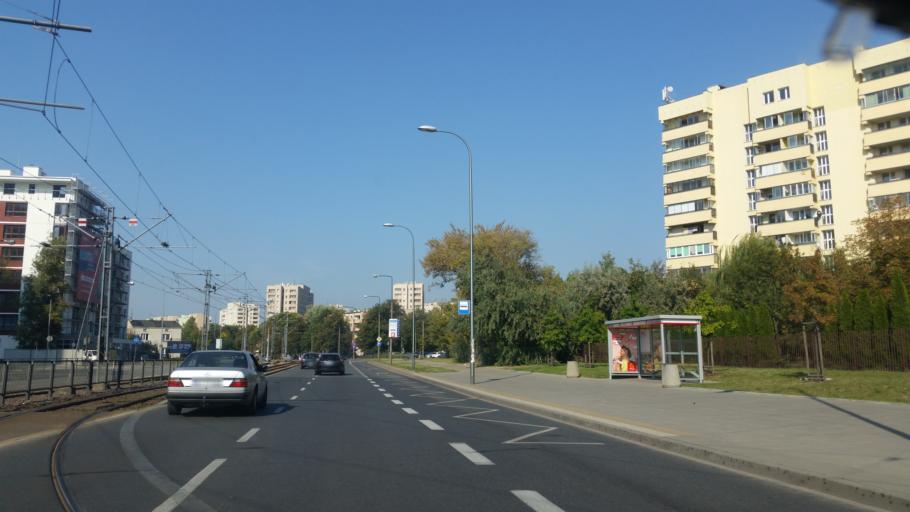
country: PL
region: Masovian Voivodeship
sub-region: Warszawa
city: Bemowo
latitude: 52.2209
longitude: 20.9169
